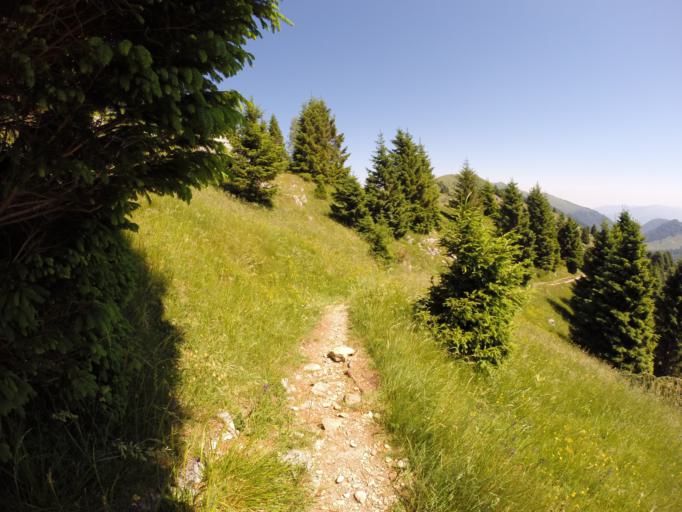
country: IT
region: Veneto
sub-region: Provincia di Treviso
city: Crespano del Grappa
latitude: 45.8923
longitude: 11.8137
